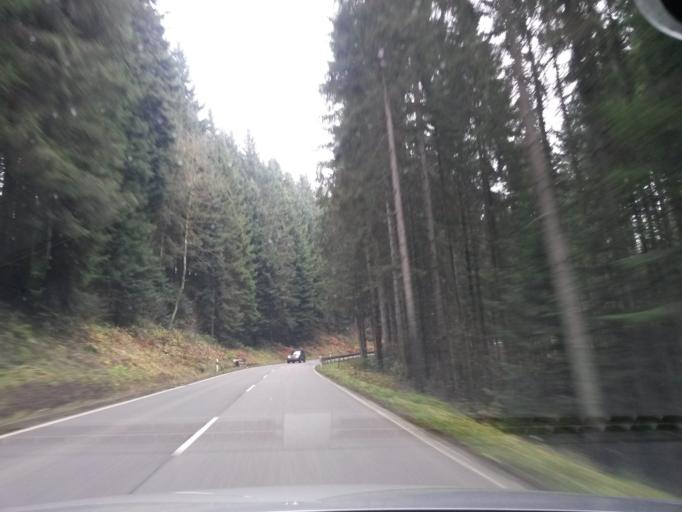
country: DE
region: Baden-Wuerttemberg
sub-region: Karlsruhe Region
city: Alpirsbach
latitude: 48.3452
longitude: 8.4543
